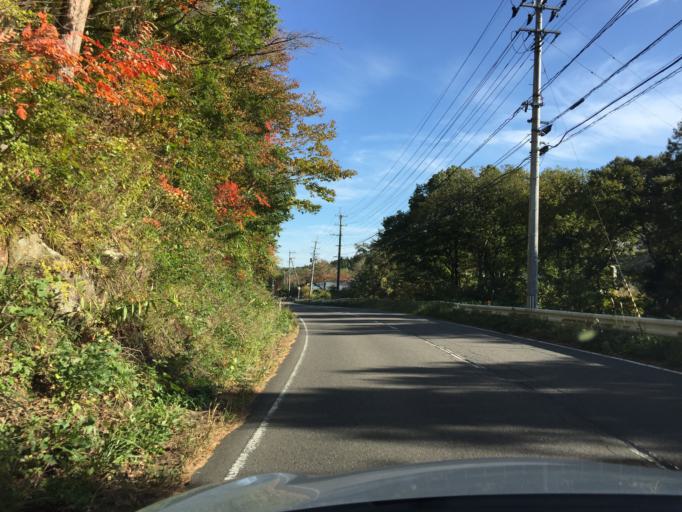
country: JP
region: Fukushima
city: Funehikimachi-funehiki
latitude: 37.3319
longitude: 140.5844
